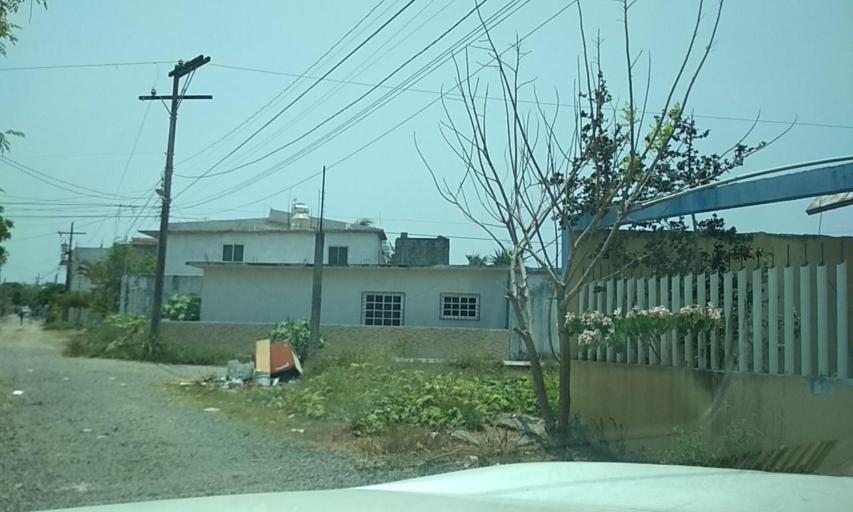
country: MX
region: Veracruz
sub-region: Veracruz
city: Las Amapolas
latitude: 19.1591
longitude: -96.1876
